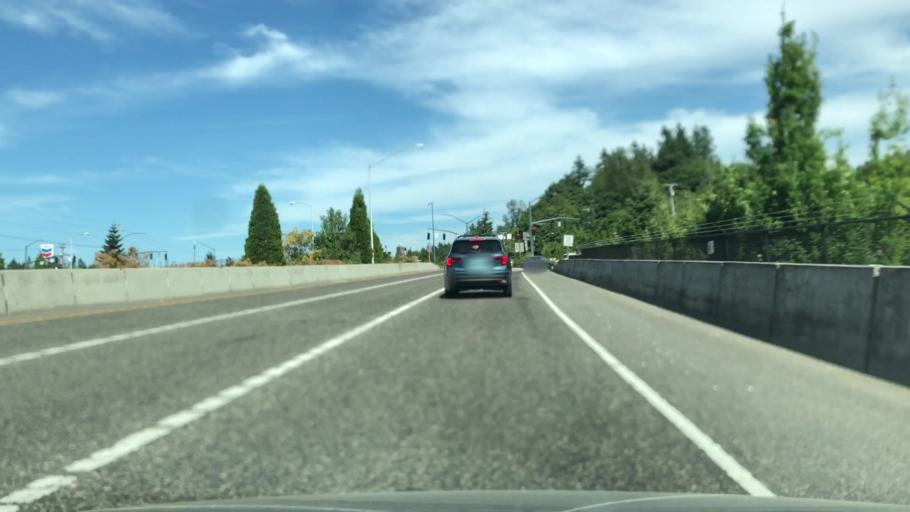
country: US
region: Oregon
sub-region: Washington County
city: West Slope
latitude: 45.5084
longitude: -122.7381
